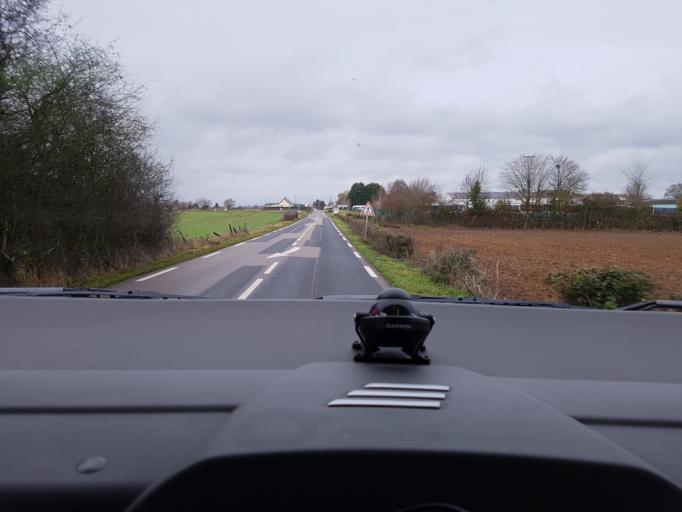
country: FR
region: Haute-Normandie
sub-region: Departement de la Seine-Maritime
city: Gournay-en-Bray
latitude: 49.4716
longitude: 1.7098
